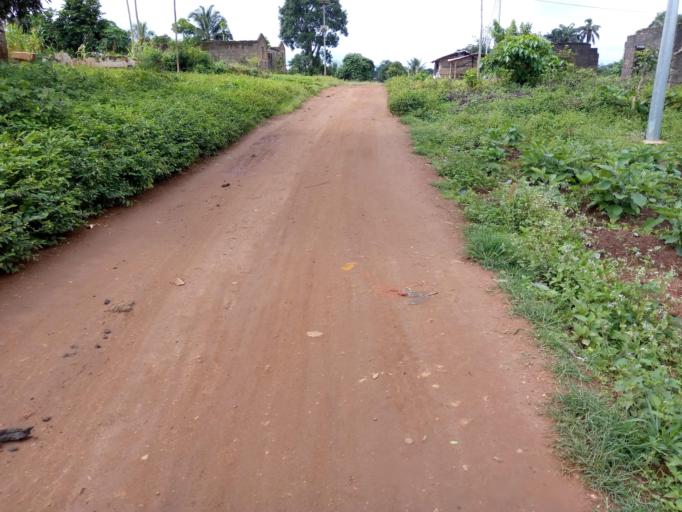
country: SL
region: Eastern Province
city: Buedu
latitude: 8.4597
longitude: -10.3346
